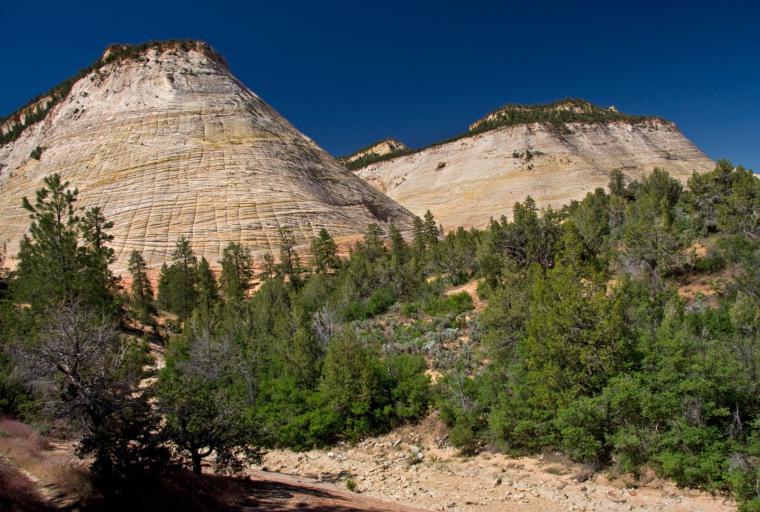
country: US
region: Utah
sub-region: Washington County
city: Hildale
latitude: 37.2304
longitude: -112.8787
